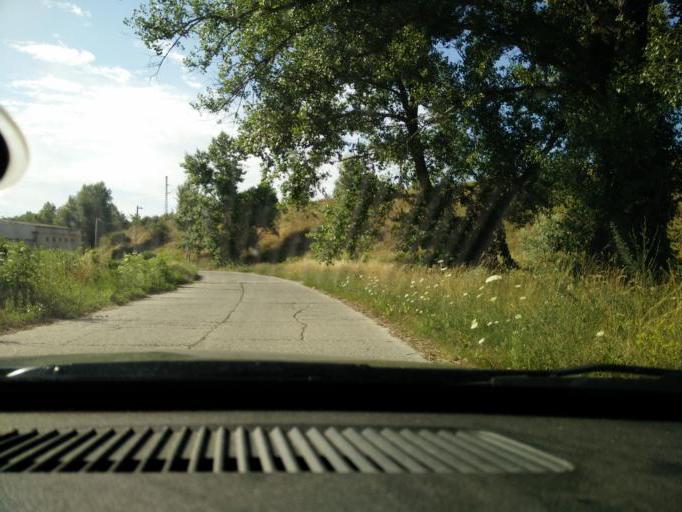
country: HU
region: Komarom-Esztergom
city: Tatabanya
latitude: 47.5605
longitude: 18.4463
